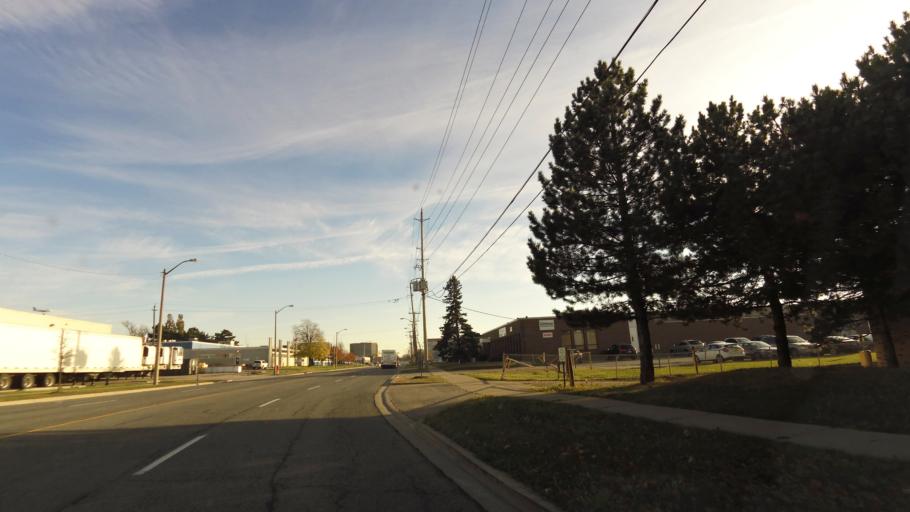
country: CA
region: Ontario
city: Etobicoke
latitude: 43.6959
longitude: -79.5898
